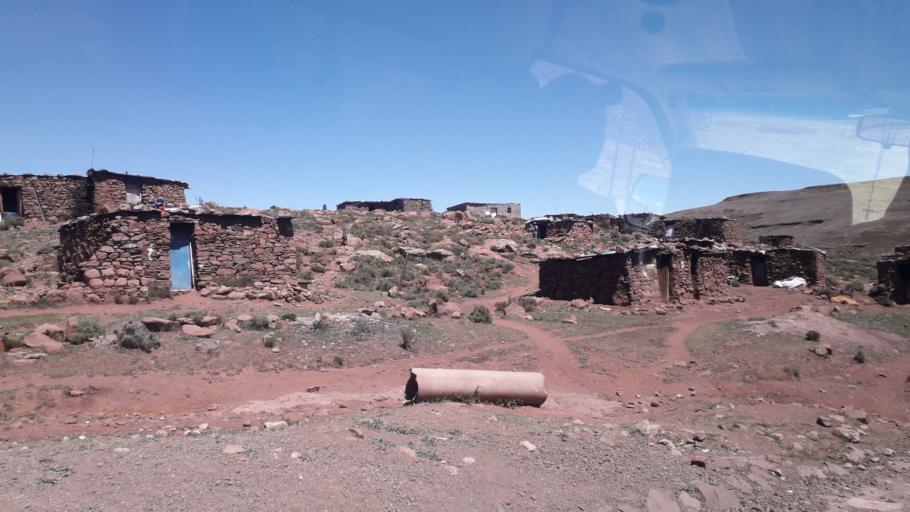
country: LS
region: Mokhotlong
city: Mokhotlong
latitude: -29.0125
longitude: 28.8441
